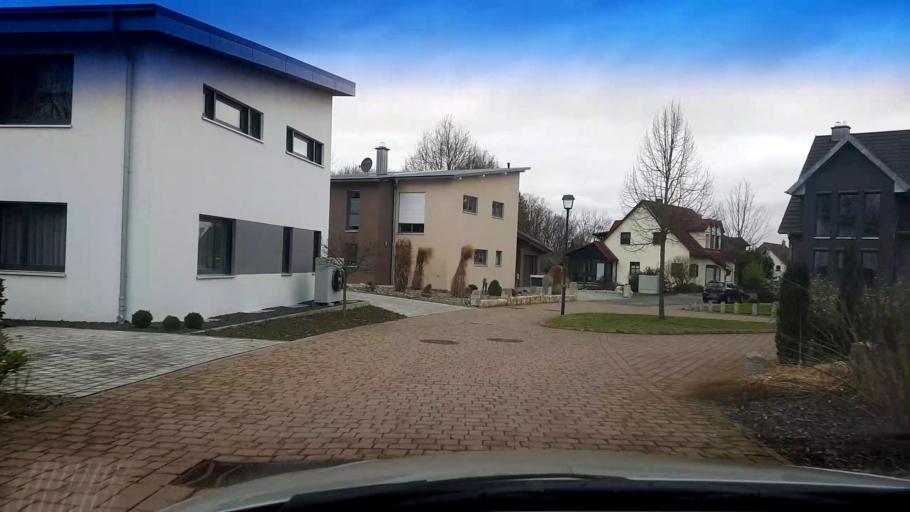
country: DE
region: Bavaria
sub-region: Upper Franconia
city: Baunach
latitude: 49.9785
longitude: 10.8484
